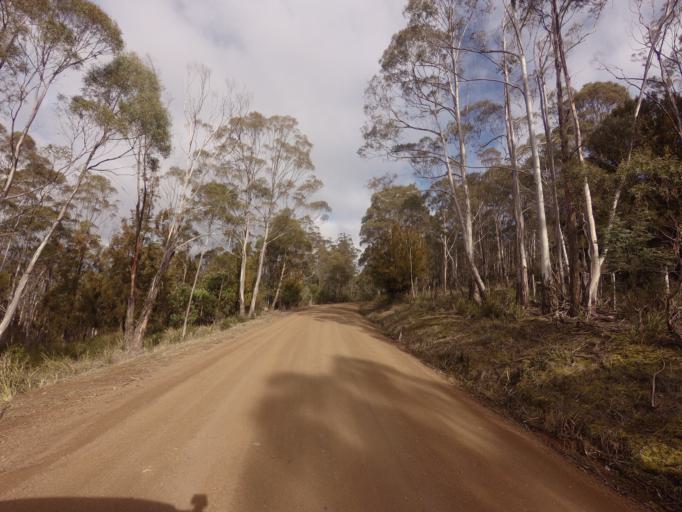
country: AU
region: Tasmania
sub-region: Derwent Valley
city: New Norfolk
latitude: -42.7866
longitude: 146.9381
